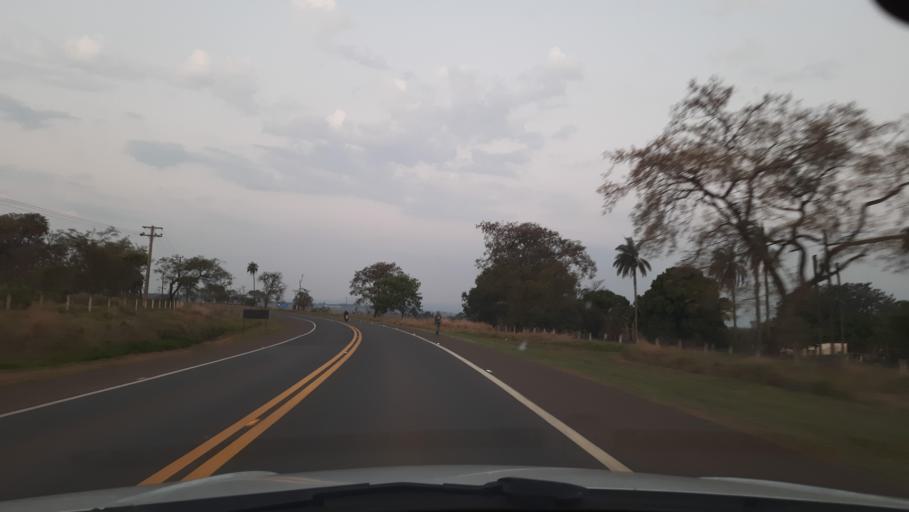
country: BR
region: Sao Paulo
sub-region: Casa Branca
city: Casa Branca
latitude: -21.7980
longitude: -47.0777
